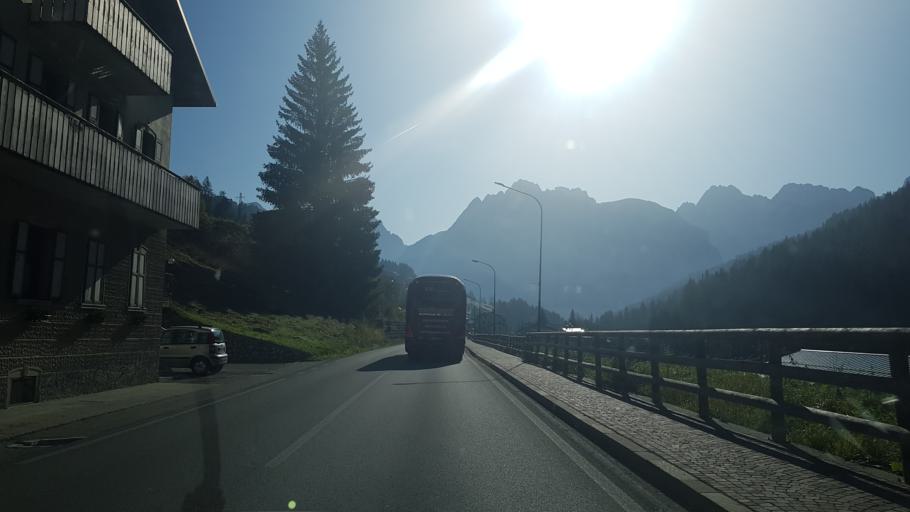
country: IT
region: Veneto
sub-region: Provincia di Belluno
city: San Nicolo Comelico
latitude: 46.5799
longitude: 12.5276
